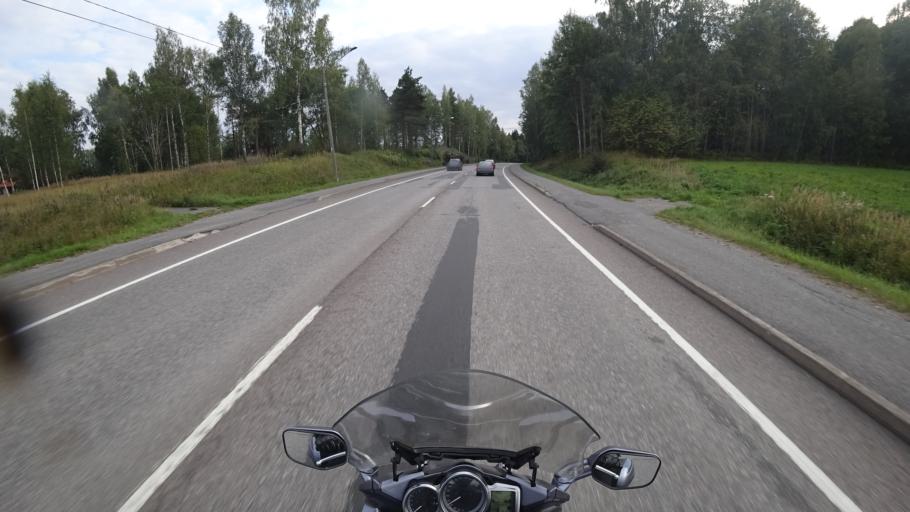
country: FI
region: Uusimaa
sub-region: Raaseporin
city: Karis
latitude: 60.0794
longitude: 23.6617
